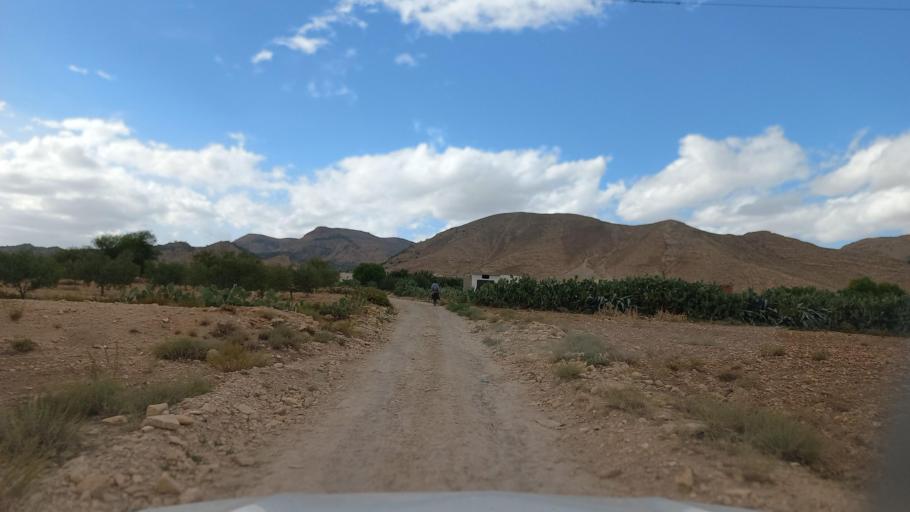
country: TN
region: Al Qasrayn
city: Sbiba
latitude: 35.4489
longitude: 9.0720
